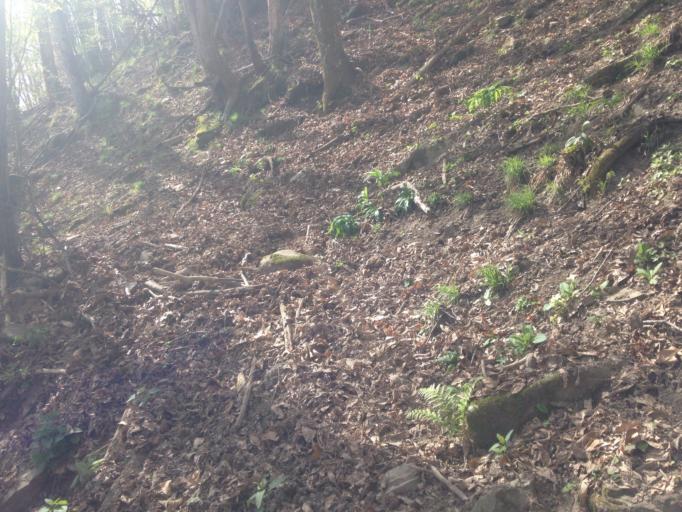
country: IT
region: Emilia-Romagna
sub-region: Provincia di Bologna
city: Lizzano in Belvedere
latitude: 44.1574
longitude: 10.8882
